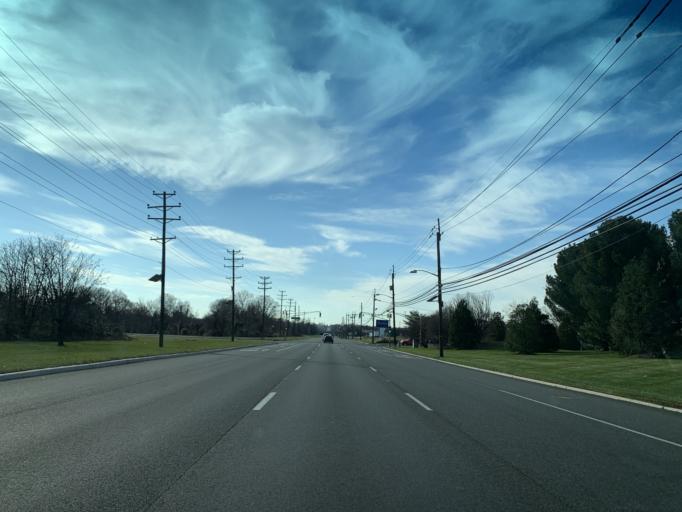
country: US
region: New Jersey
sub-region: Burlington County
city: Palmyra
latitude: 39.9774
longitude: -75.0308
